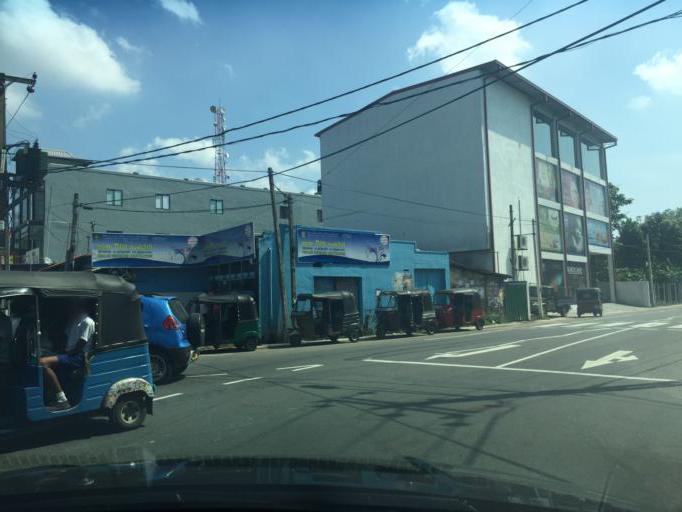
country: LK
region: Western
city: Sri Jayewardenepura Kotte
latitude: 6.8695
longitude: 79.8978
